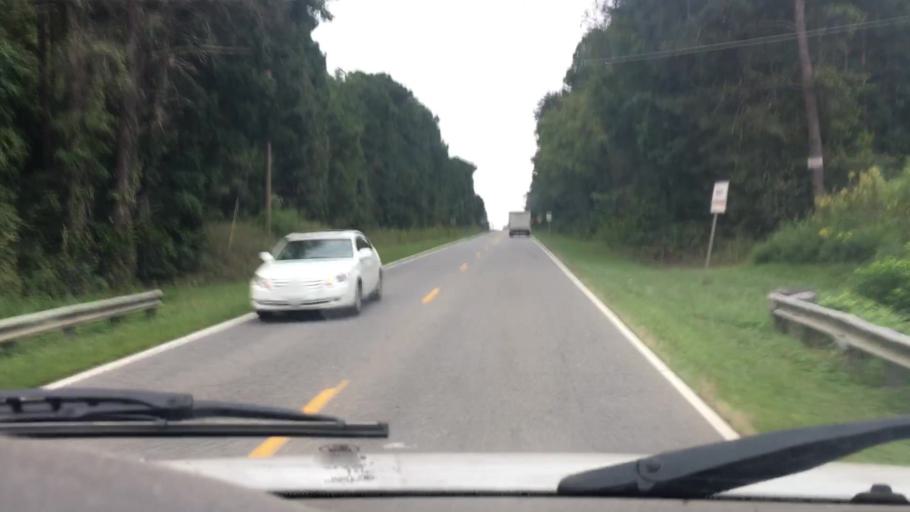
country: US
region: North Carolina
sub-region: Catawba County
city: Lake Norman of Catawba
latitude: 35.5647
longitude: -80.9904
